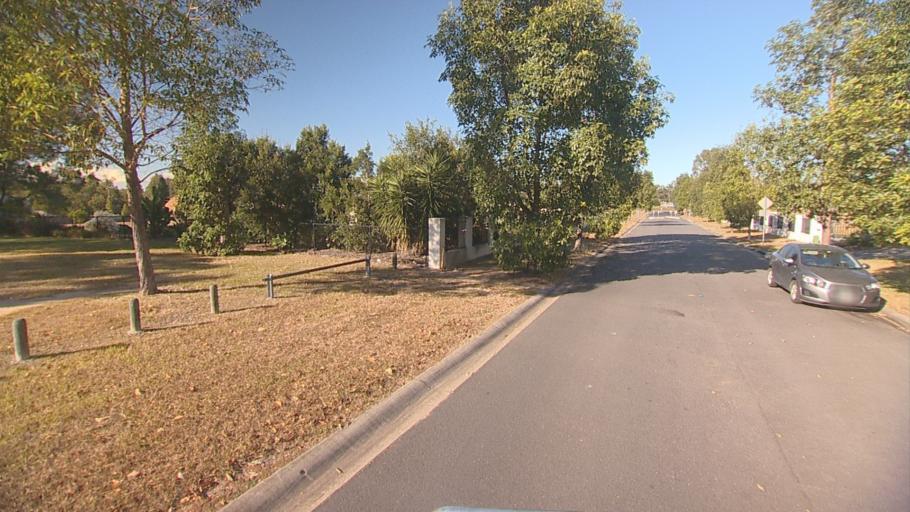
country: AU
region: Queensland
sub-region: Brisbane
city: Forest Lake
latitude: -27.6543
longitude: 152.9879
